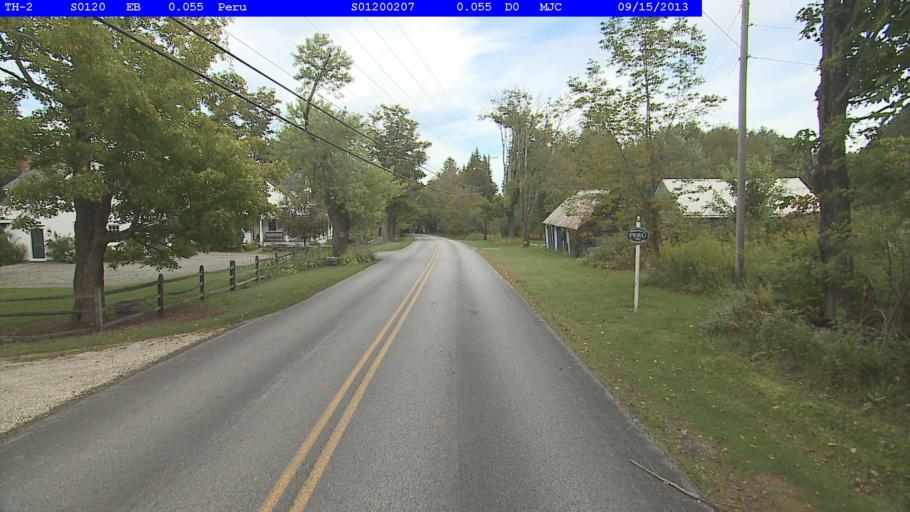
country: US
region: Vermont
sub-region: Bennington County
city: Manchester Center
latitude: 43.2280
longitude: -72.9028
